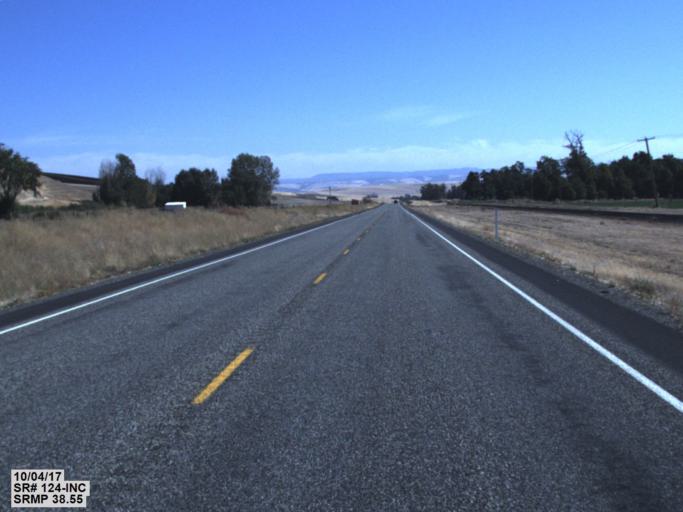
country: US
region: Washington
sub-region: Walla Walla County
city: Waitsburg
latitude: 46.2934
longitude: -118.2663
